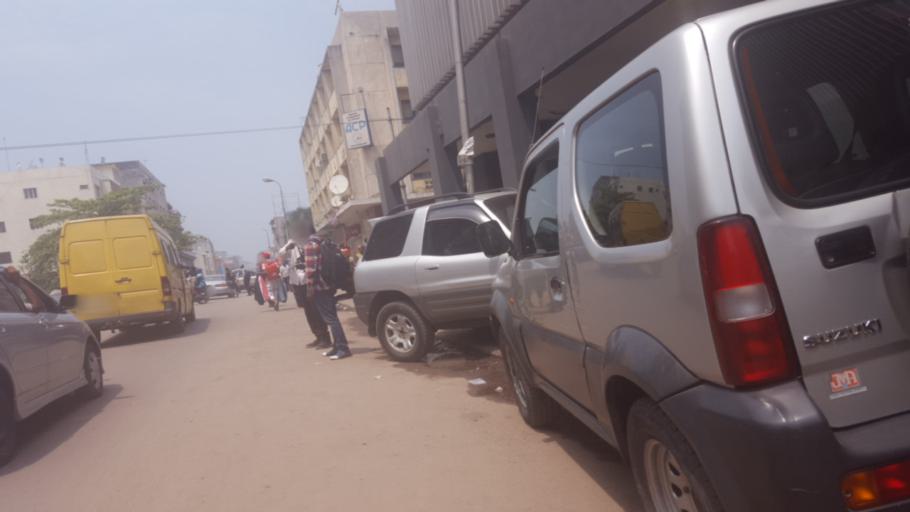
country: CD
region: Kinshasa
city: Kinshasa
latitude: -4.3067
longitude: 15.3099
